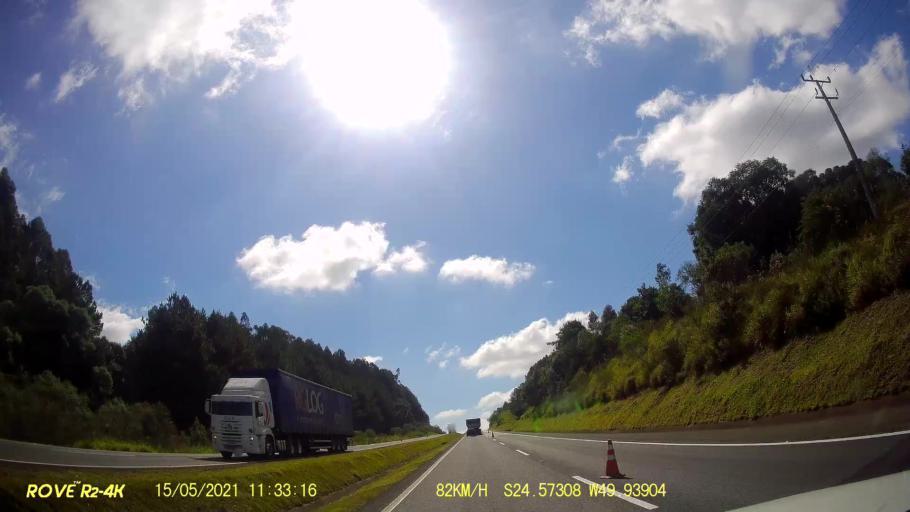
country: BR
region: Parana
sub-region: Pirai Do Sul
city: Pirai do Sul
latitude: -24.5730
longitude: -49.9390
